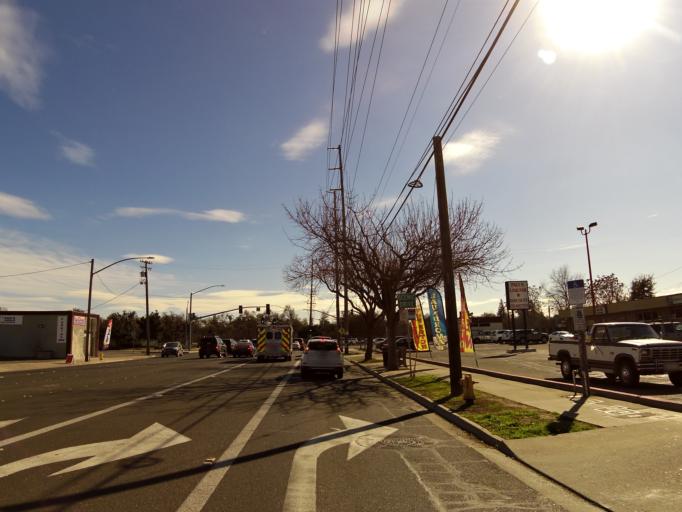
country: US
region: California
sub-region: Stanislaus County
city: Modesto
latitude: 37.6499
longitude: -120.9757
